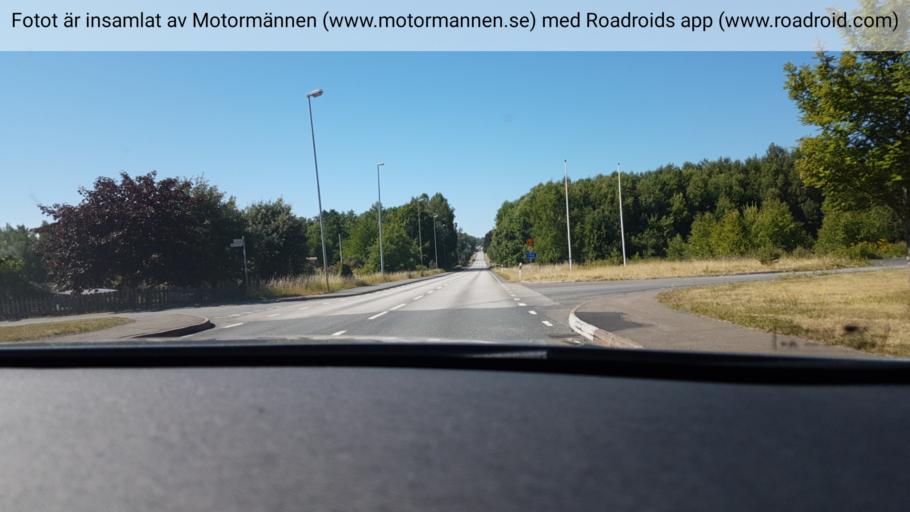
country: SE
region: Vaestra Goetaland
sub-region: Hjo Kommun
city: Hjo
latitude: 58.0959
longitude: 14.2049
